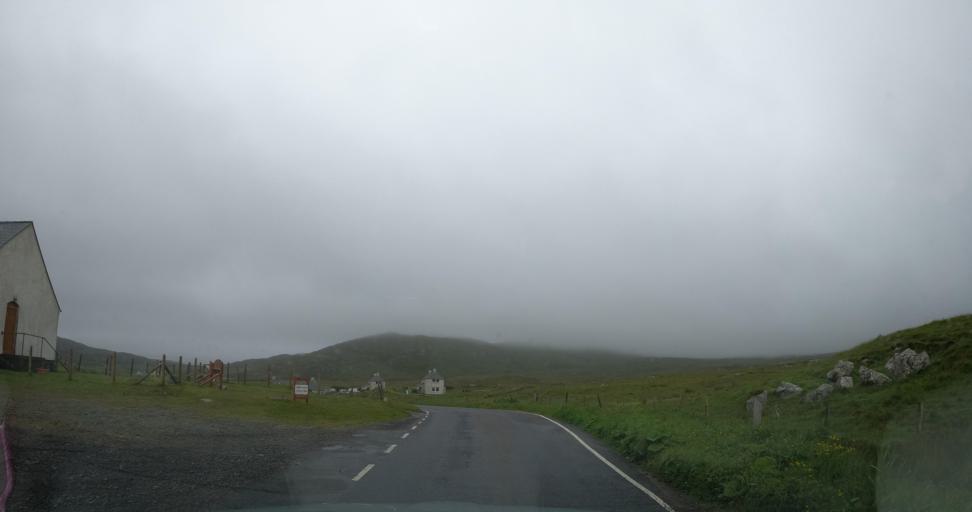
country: GB
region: Scotland
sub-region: Eilean Siar
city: Barra
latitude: 57.0011
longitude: -7.4859
